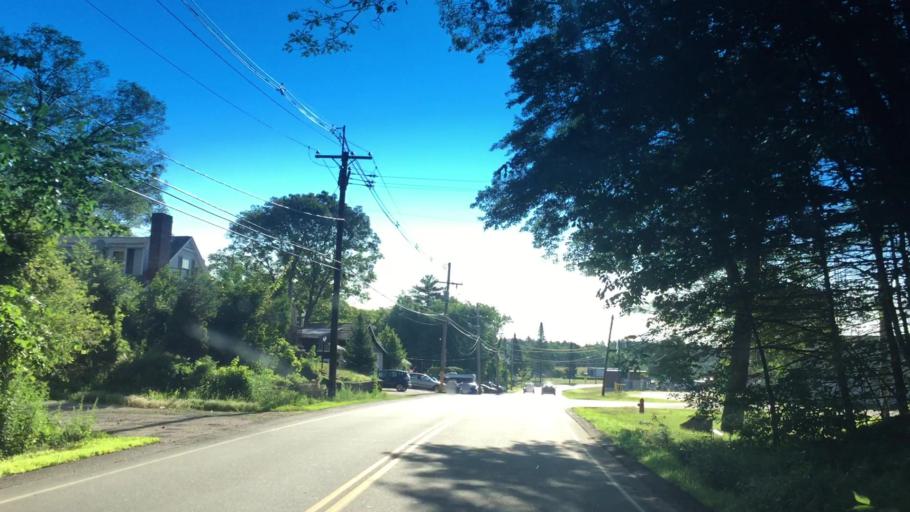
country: US
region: Massachusetts
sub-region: Norfolk County
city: Norfolk
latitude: 42.1212
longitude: -71.3069
